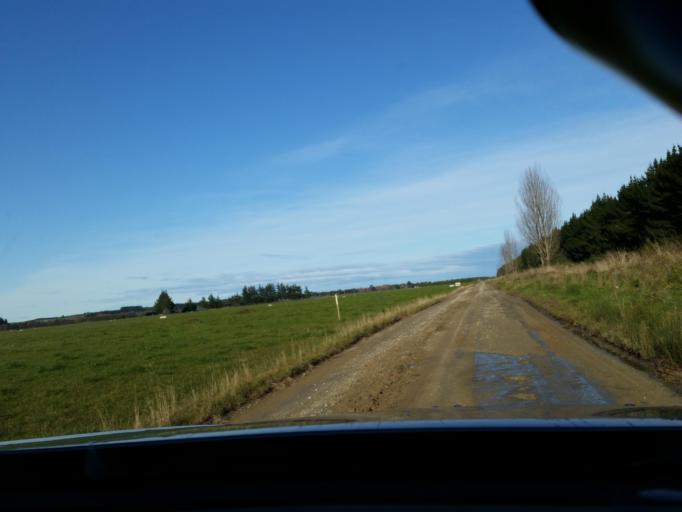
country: NZ
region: Southland
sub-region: Southland District
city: Winton
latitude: -46.2256
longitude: 168.4903
